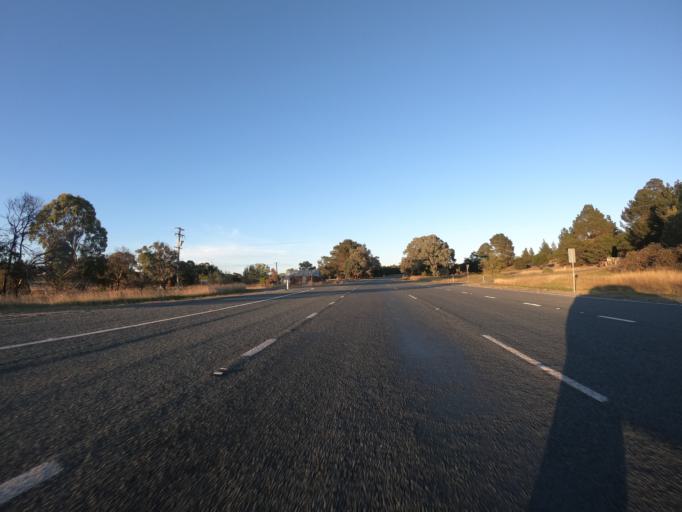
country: AU
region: New South Wales
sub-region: Goulburn Mulwaree
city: Goulburn
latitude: -34.8269
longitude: 149.5972
